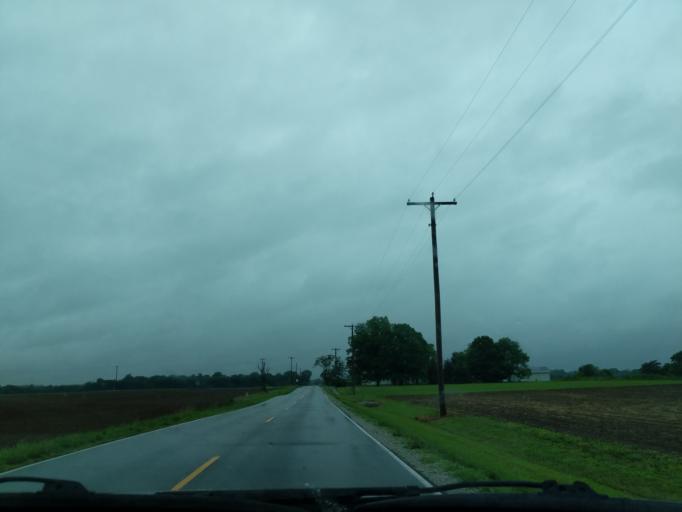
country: US
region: Indiana
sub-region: Madison County
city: Lapel
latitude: 40.0665
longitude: -85.9079
